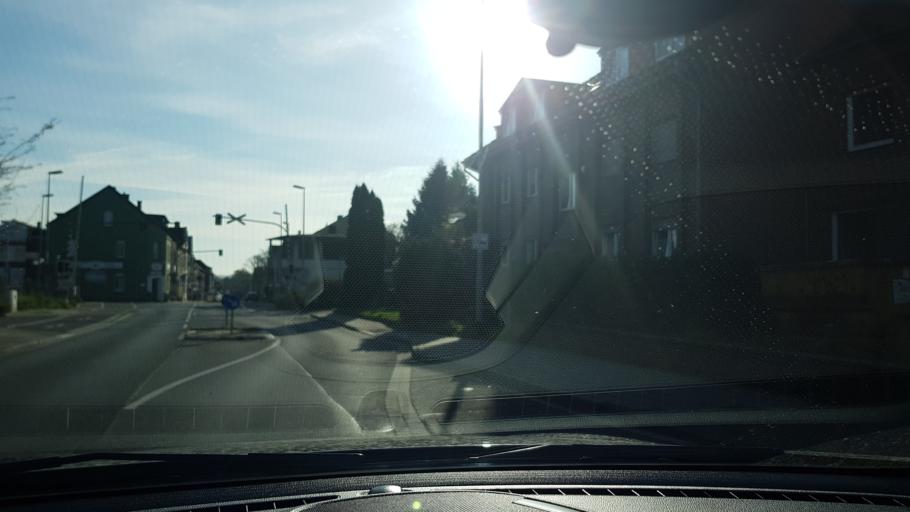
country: DE
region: North Rhine-Westphalia
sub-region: Regierungsbezirk Dusseldorf
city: Neubrueck
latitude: 51.1303
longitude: 6.6206
